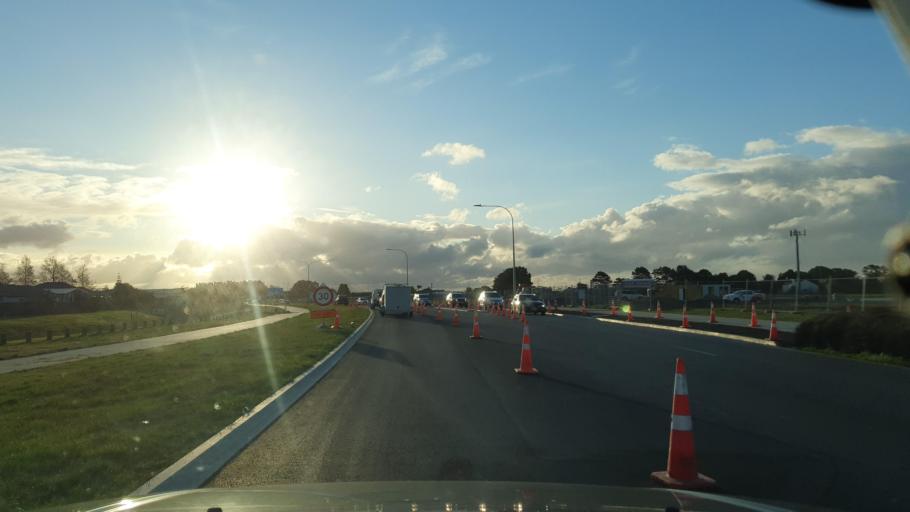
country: NZ
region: Bay of Plenty
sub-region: Western Bay of Plenty District
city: Maketu
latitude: -37.7151
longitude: 176.3128
